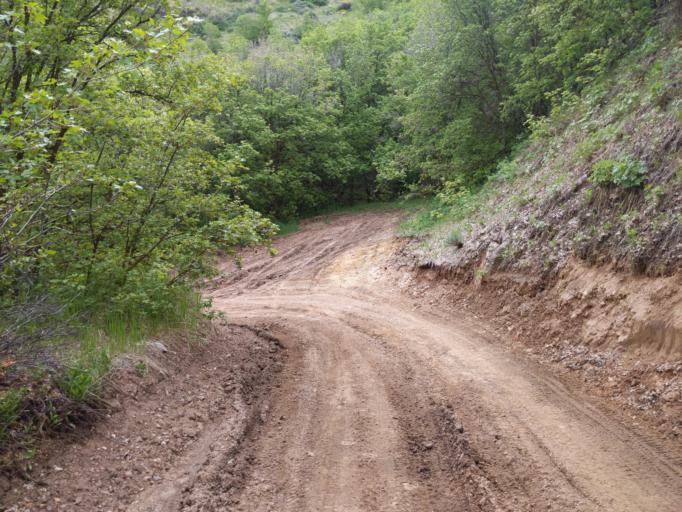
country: US
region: Idaho
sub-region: Bannock County
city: Pocatello
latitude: 42.8232
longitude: -112.4838
